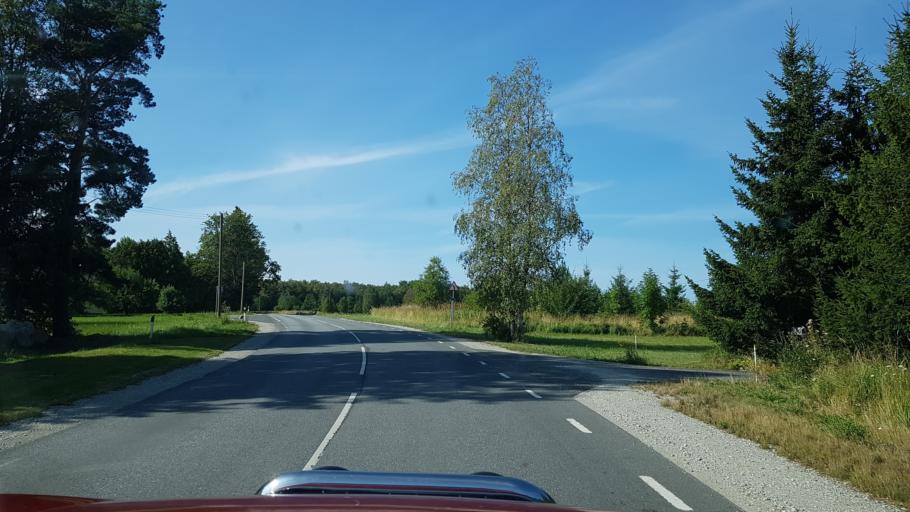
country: EE
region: Harju
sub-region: Rae vald
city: Jueri
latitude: 59.3830
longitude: 24.9290
